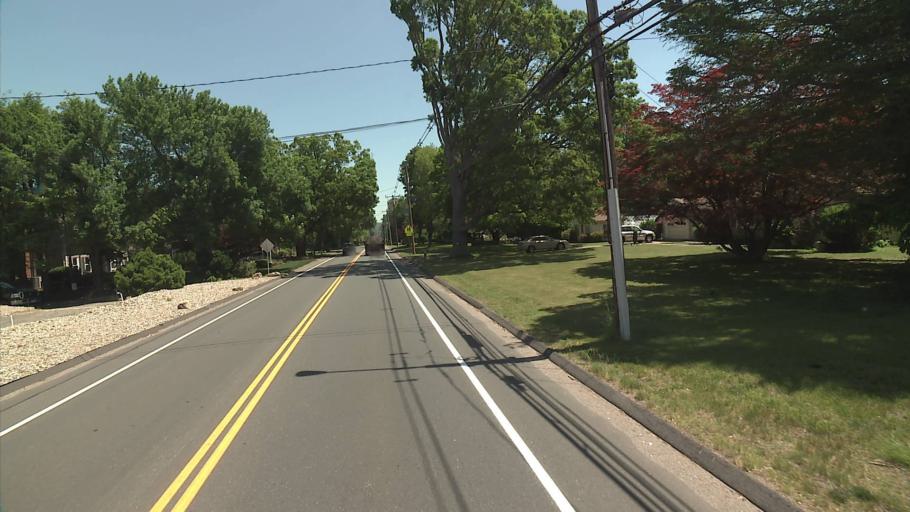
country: US
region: Connecticut
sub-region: Tolland County
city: Rockville
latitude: 41.8545
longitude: -72.4422
